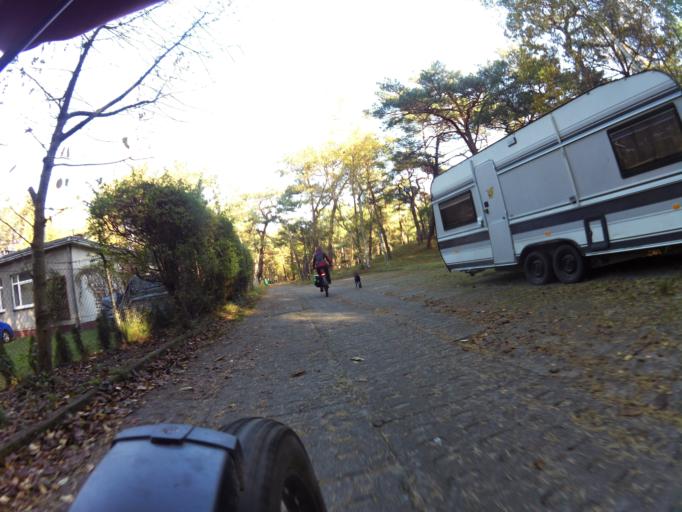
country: PL
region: Pomeranian Voivodeship
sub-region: Powiat pucki
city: Hel
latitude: 54.6019
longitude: 18.8135
